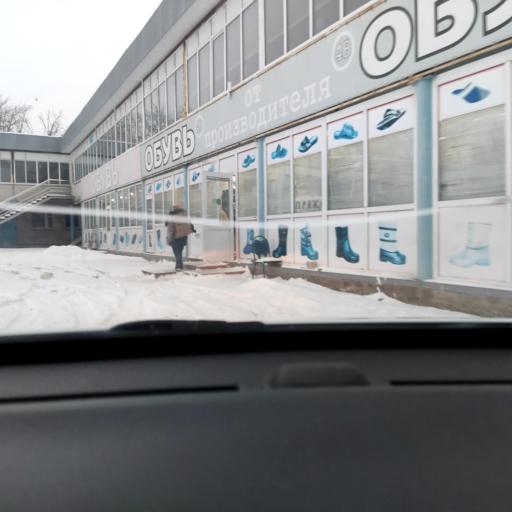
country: RU
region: Voronezj
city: Somovo
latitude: 51.6815
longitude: 39.2980
